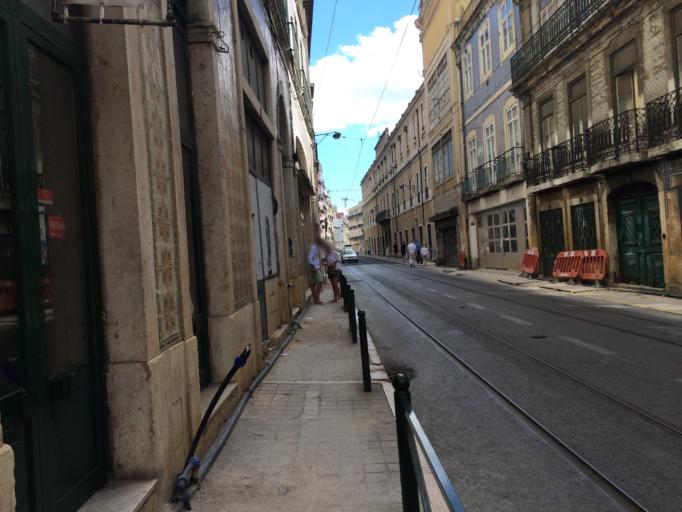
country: PT
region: Lisbon
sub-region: Lisbon
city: Lisbon
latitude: 38.7088
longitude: -9.1494
